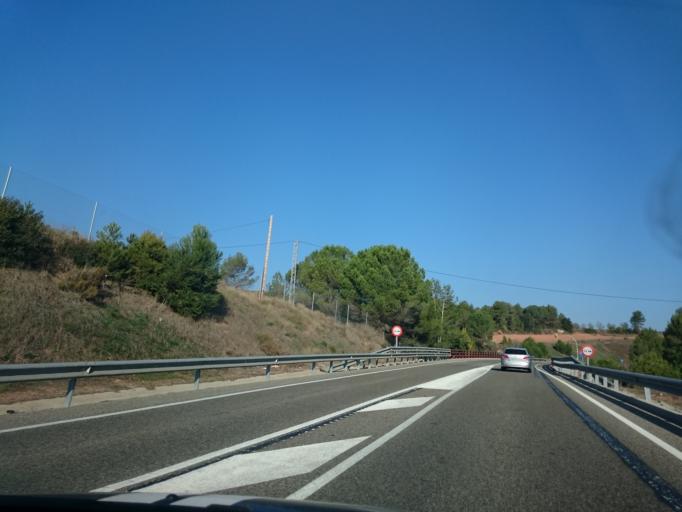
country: ES
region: Catalonia
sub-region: Provincia de Barcelona
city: Sant Salvador de Guardiola
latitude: 41.6788
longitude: 1.7540
